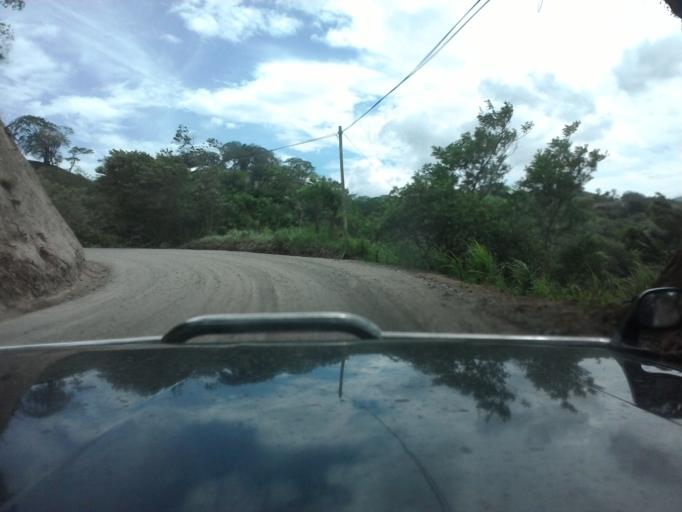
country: CR
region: Guanacaste
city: Juntas
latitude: 10.2261
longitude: -84.8506
